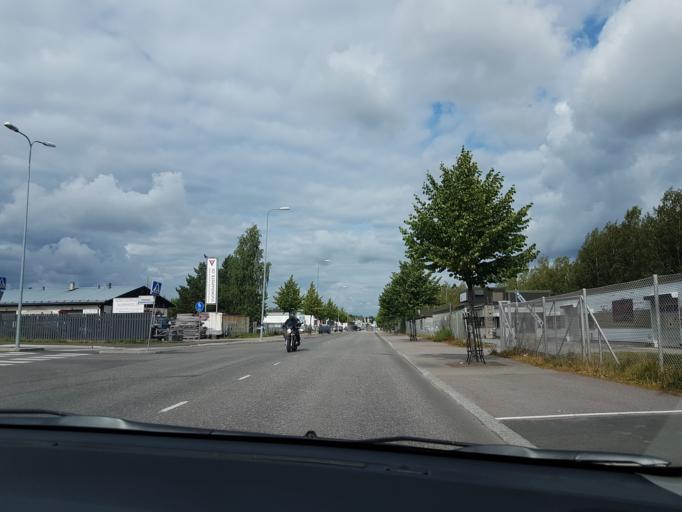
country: FI
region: Uusimaa
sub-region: Helsinki
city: Jaervenpaeae
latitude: 60.4711
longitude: 25.1185
